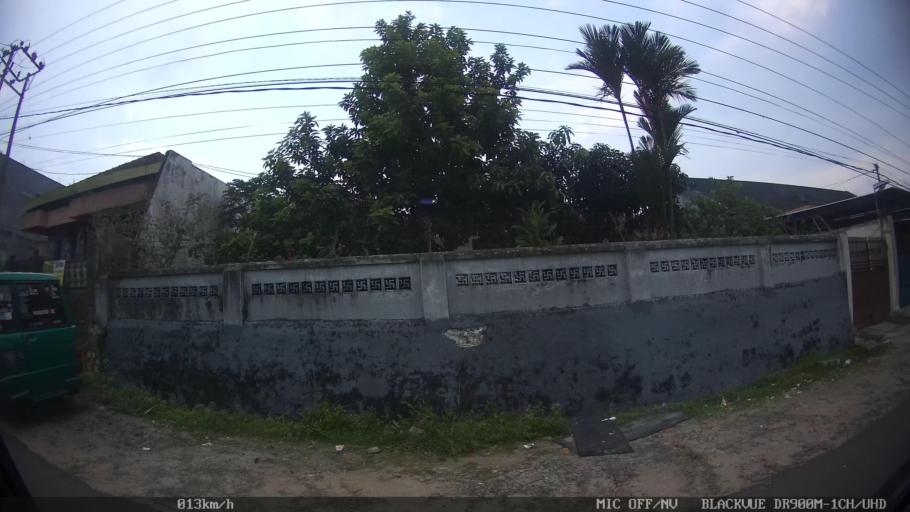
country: ID
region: Lampung
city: Bandarlampung
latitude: -5.4244
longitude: 105.2601
